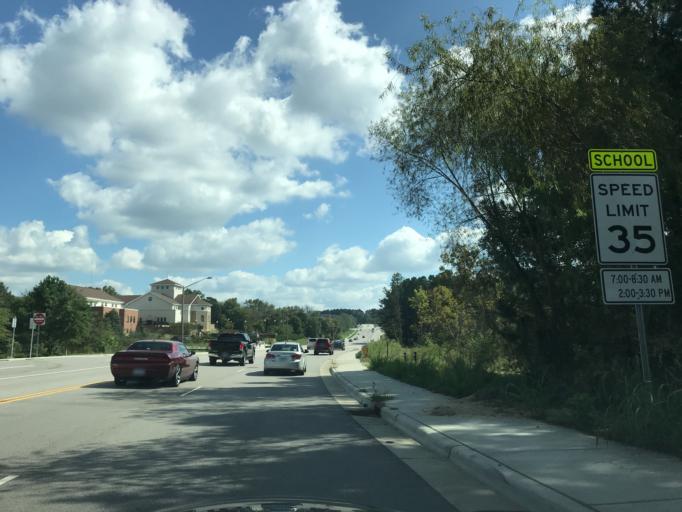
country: US
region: North Carolina
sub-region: Wake County
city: Wake Forest
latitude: 35.9499
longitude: -78.5095
